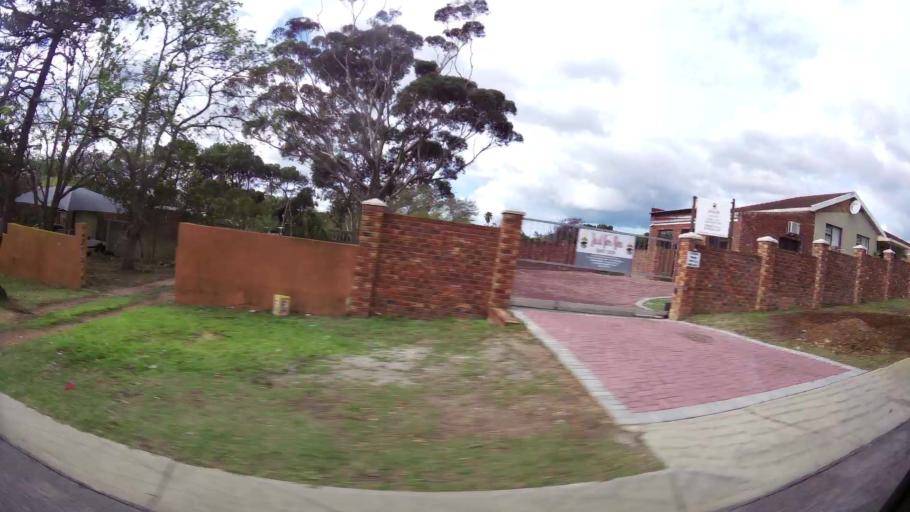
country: ZA
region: Eastern Cape
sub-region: Nelson Mandela Bay Metropolitan Municipality
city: Port Elizabeth
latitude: -33.9327
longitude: 25.5159
